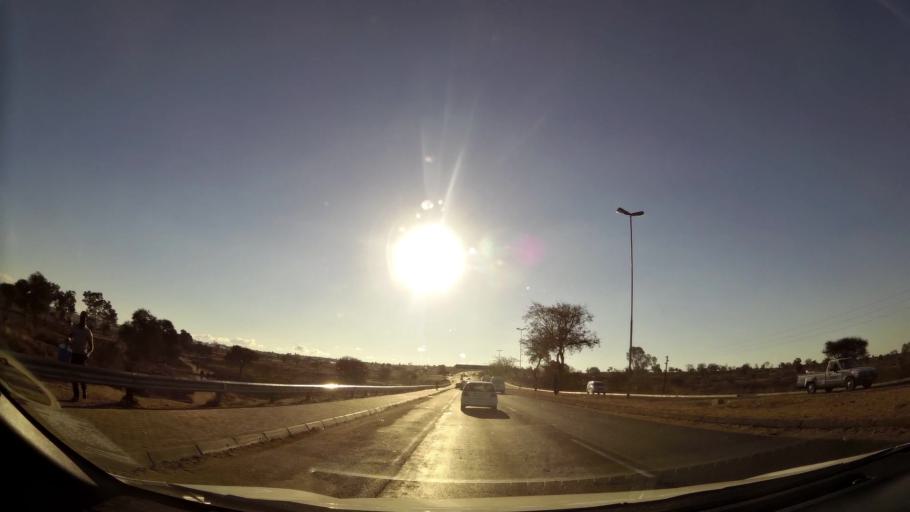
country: ZA
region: Limpopo
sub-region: Capricorn District Municipality
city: Polokwane
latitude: -23.8859
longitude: 29.4275
